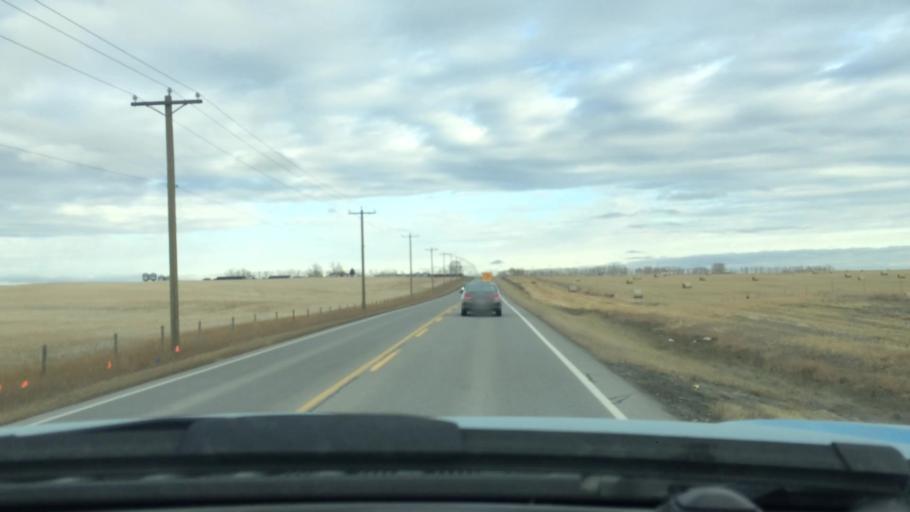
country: CA
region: Alberta
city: Airdrie
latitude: 51.2201
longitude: -114.0249
